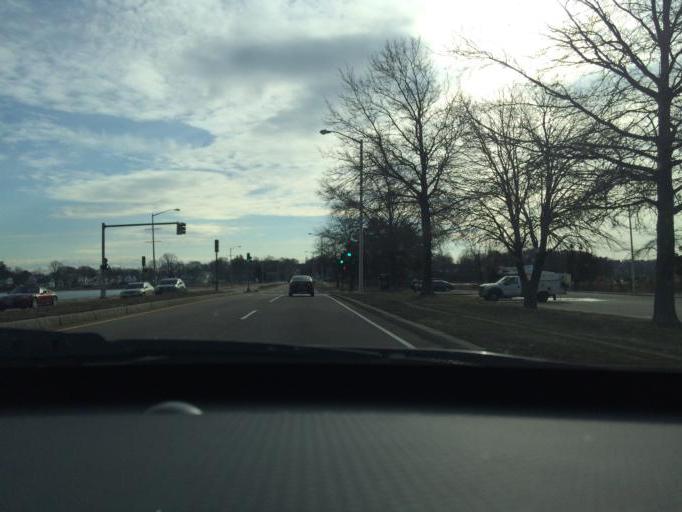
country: US
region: Massachusetts
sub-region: Norfolk County
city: Quincy
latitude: 42.2690
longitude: -70.9971
